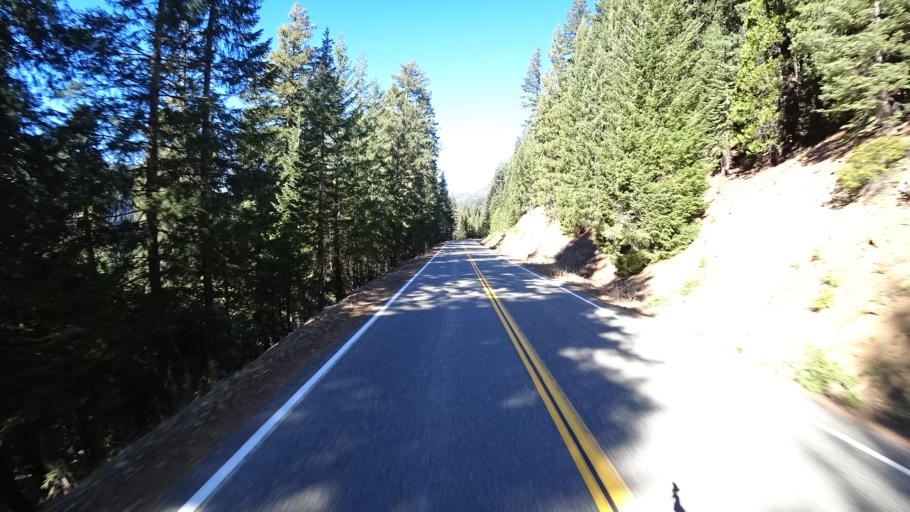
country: US
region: California
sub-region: Trinity County
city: Weaverville
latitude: 41.2233
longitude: -122.9199
